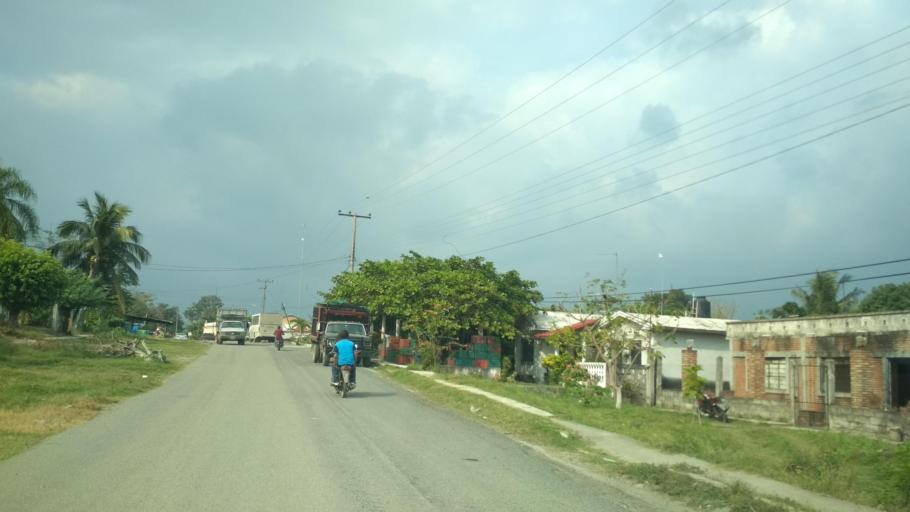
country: MM
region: Kayah
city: Loikaw
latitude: 20.2369
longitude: 97.2764
